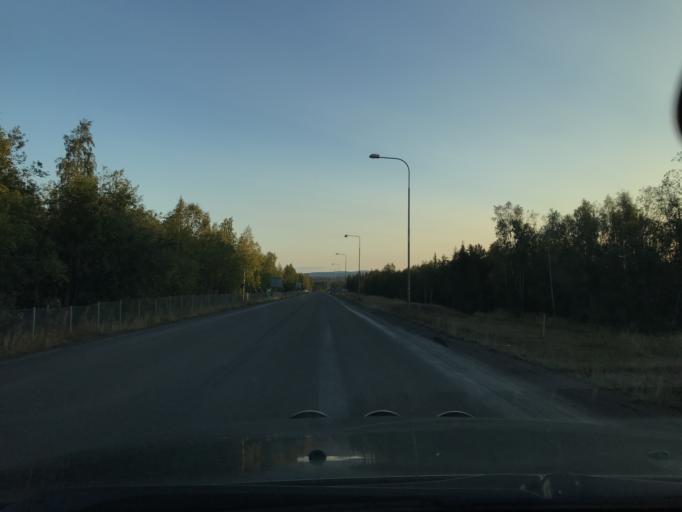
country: SE
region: Norrbotten
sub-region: Gallivare Kommun
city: Malmberget
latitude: 67.6412
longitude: 21.0178
